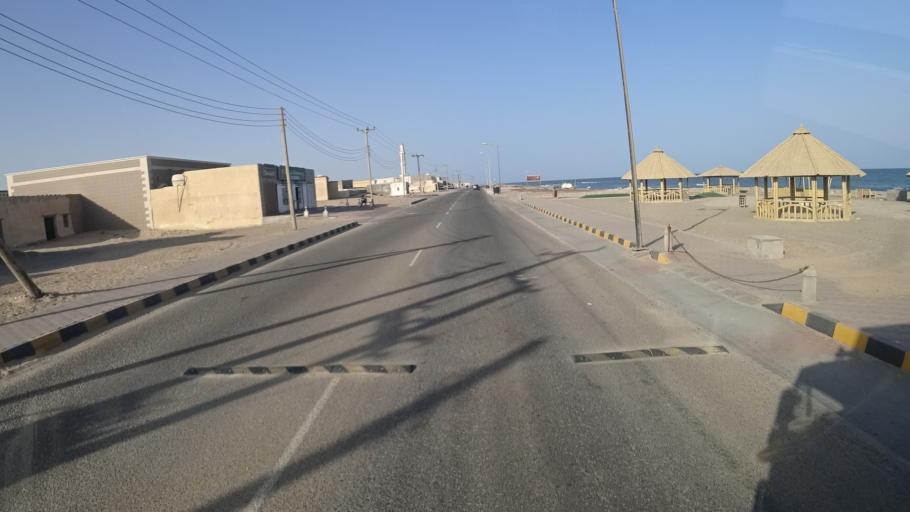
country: OM
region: Ash Sharqiyah
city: Sur
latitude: 22.1261
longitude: 59.7224
